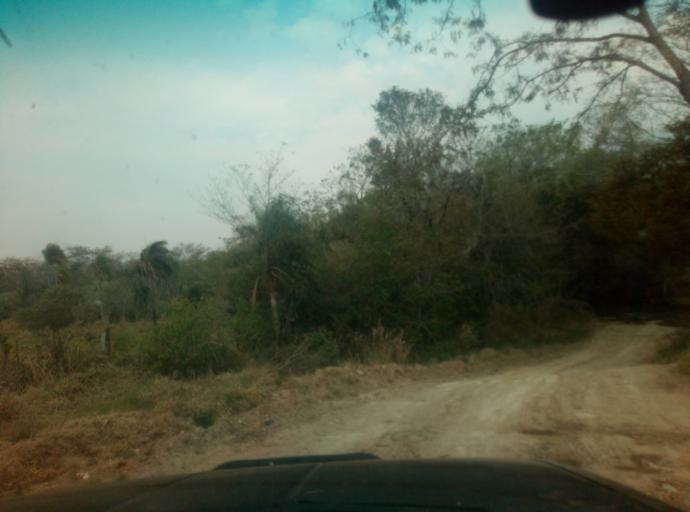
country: PY
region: Caaguazu
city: San Joaquin
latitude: -25.0845
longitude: -56.1431
